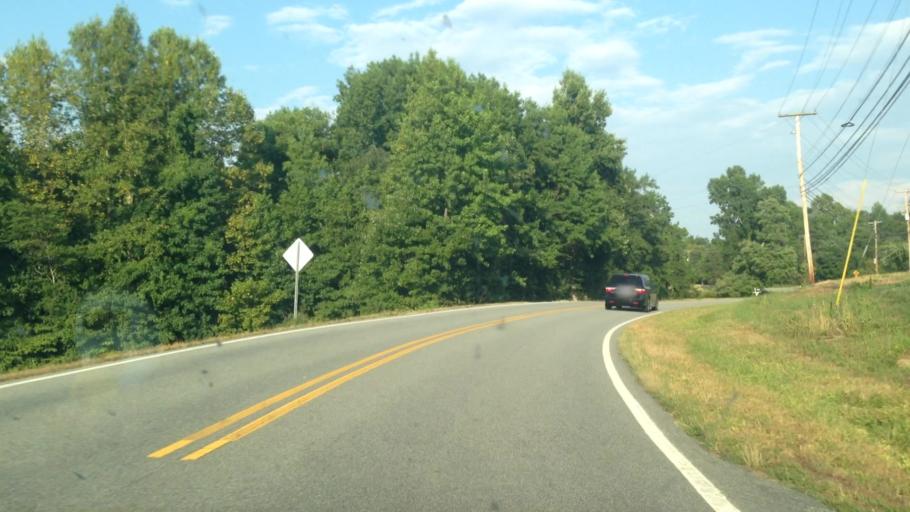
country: US
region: North Carolina
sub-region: Davidson County
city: Thomasville
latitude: 35.9403
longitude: -80.0696
